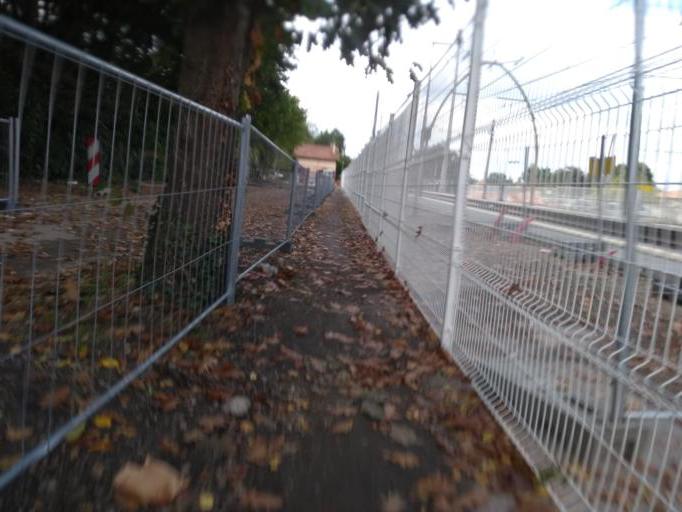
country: FR
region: Aquitaine
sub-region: Departement de la Gironde
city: Pessac
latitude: 44.7939
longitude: -0.6585
